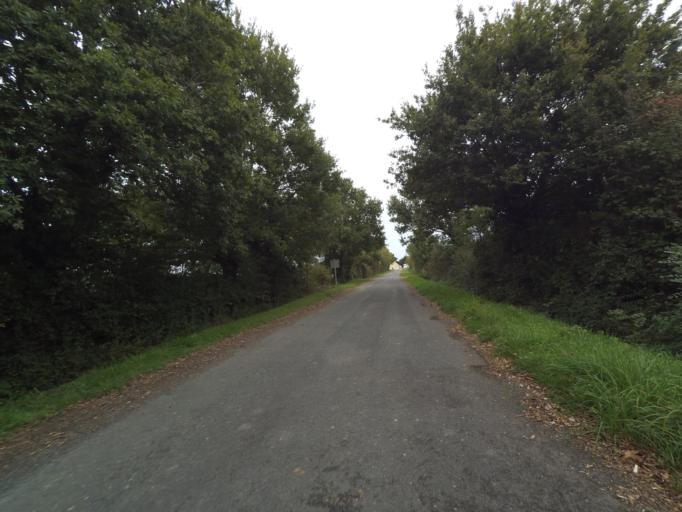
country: FR
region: Pays de la Loire
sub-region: Departement de la Vendee
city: Bouffere
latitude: 46.9806
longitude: -1.3512
